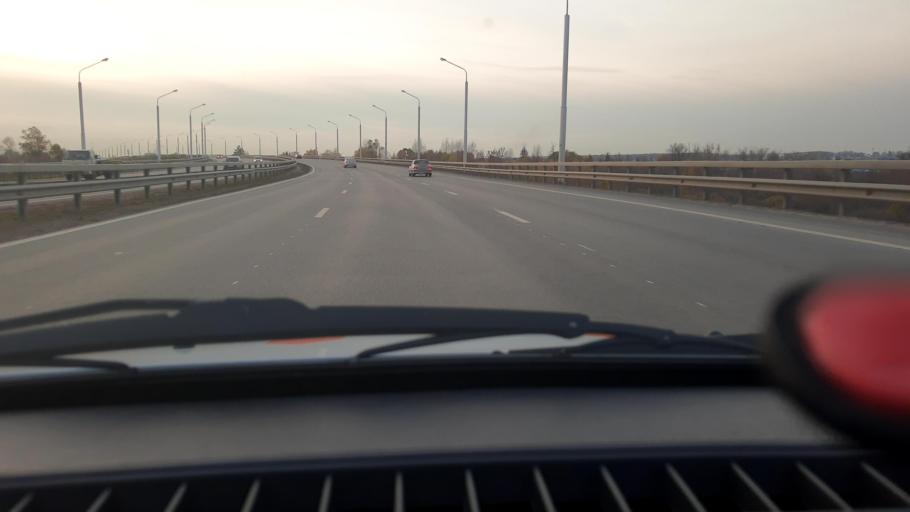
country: RU
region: Bashkortostan
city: Mikhaylovka
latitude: 54.7965
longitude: 55.9001
